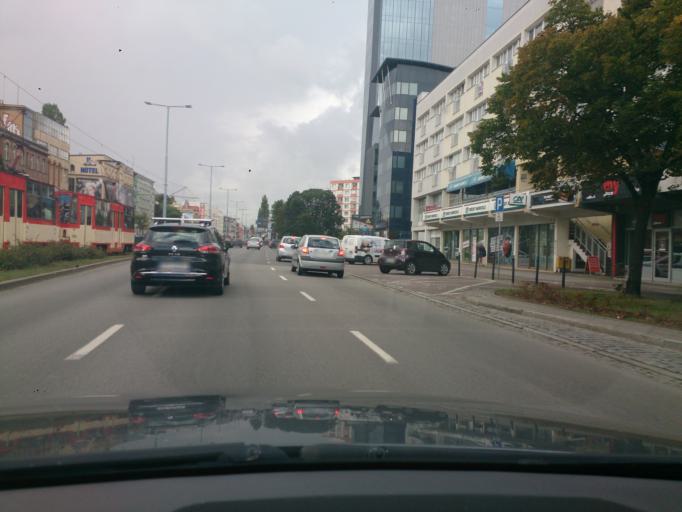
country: PL
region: Pomeranian Voivodeship
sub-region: Gdansk
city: Gdansk
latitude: 54.3786
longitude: 18.6063
